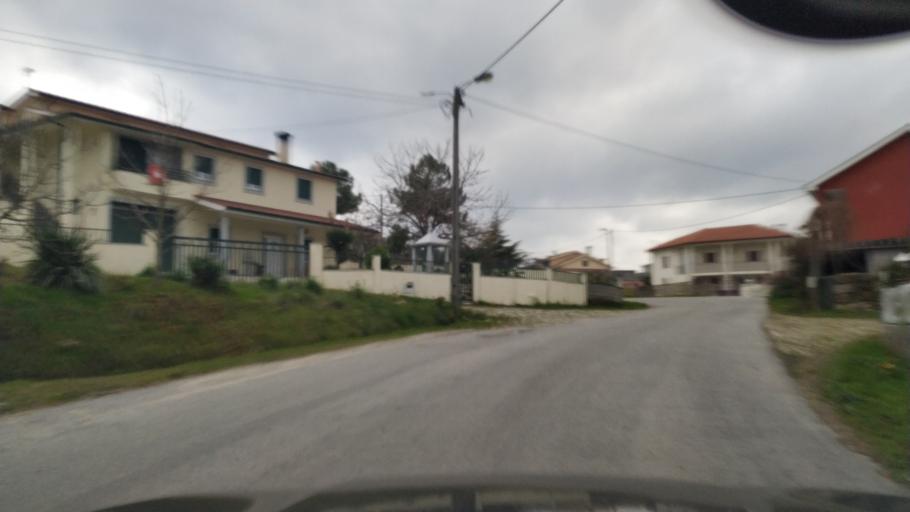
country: PT
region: Vila Real
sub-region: Sabrosa
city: Sabrosa
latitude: 41.3320
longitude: -7.6416
